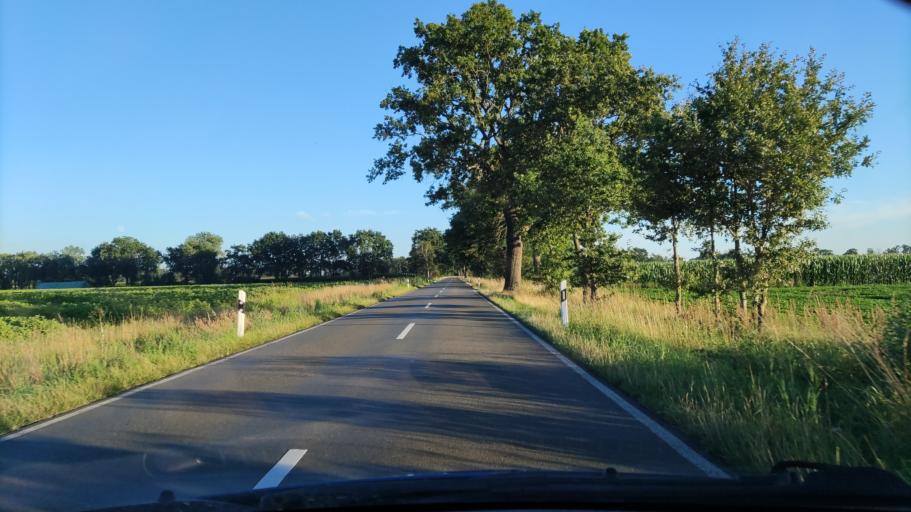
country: DE
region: Lower Saxony
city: Jameln
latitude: 53.0387
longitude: 11.1279
